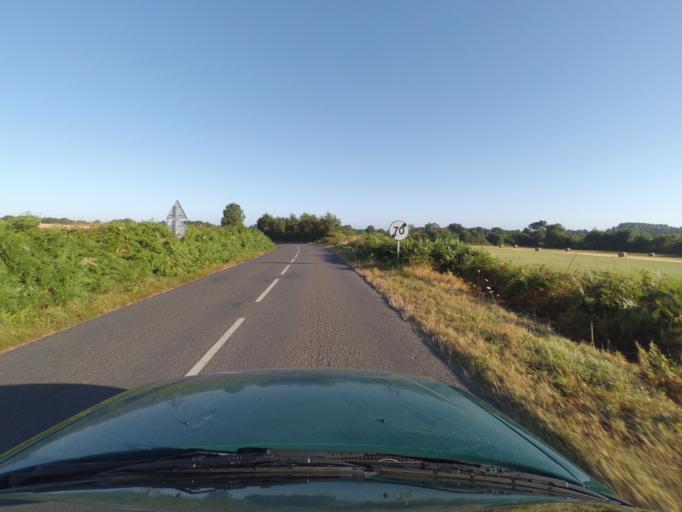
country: FR
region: Pays de la Loire
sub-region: Departement de la Loire-Atlantique
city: Montbert
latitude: 47.0413
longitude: -1.4730
